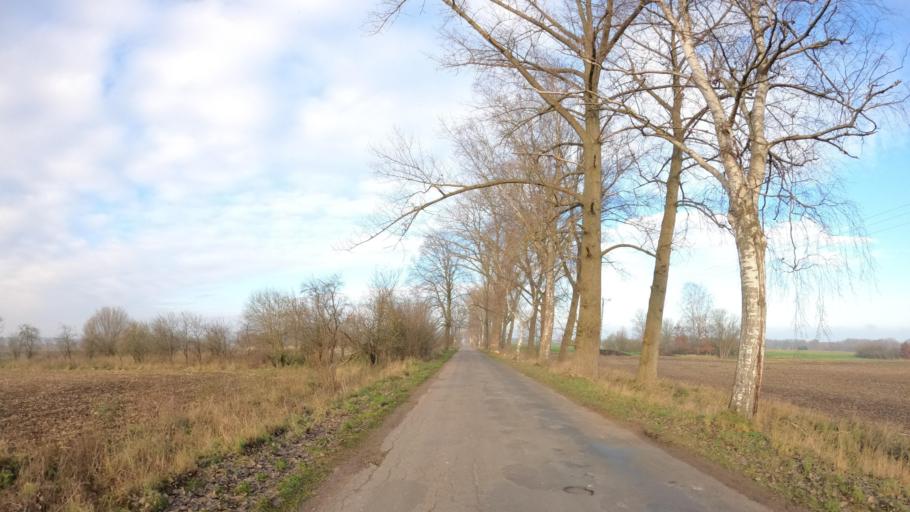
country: PL
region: West Pomeranian Voivodeship
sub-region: Powiat goleniowski
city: Maszewo
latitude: 53.5686
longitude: 15.0910
